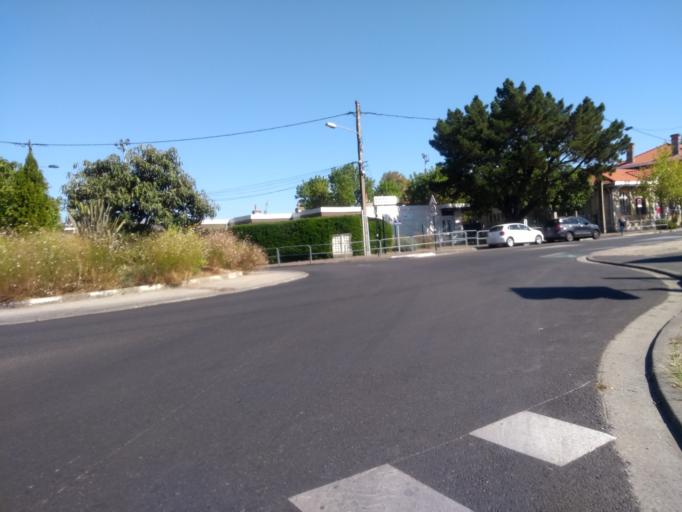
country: FR
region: Aquitaine
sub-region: Departement de la Gironde
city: Le Bouscat
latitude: 44.8431
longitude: -0.6070
